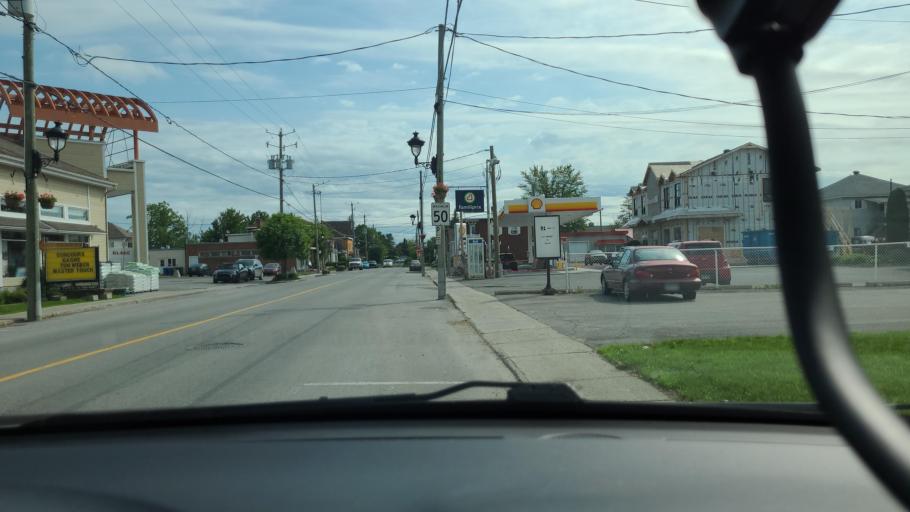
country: CA
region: Quebec
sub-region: Lanaudiere
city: Crabtree
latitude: 45.9648
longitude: -73.4730
